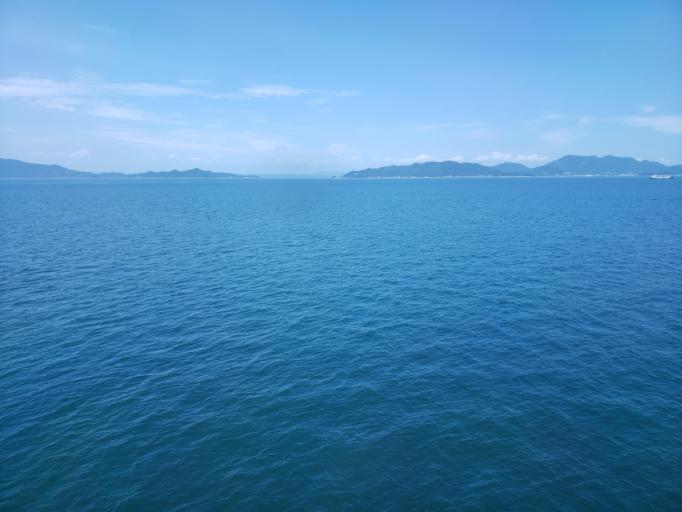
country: JP
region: Kagawa
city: Tonosho
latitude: 34.4056
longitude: 134.1460
